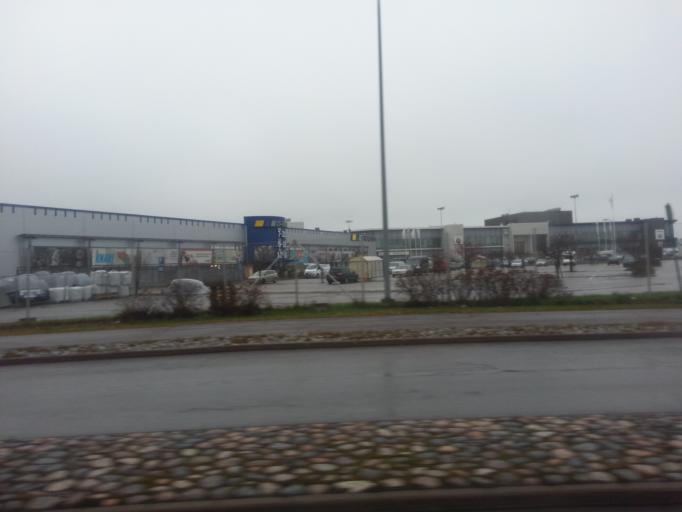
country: FI
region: Uusimaa
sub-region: Helsinki
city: Vantaa
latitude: 60.2936
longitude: 24.9523
